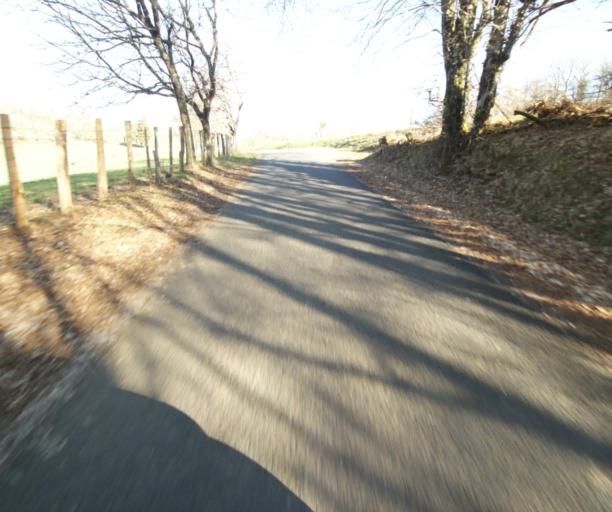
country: FR
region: Limousin
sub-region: Departement de la Correze
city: Seilhac
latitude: 45.3701
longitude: 1.7521
